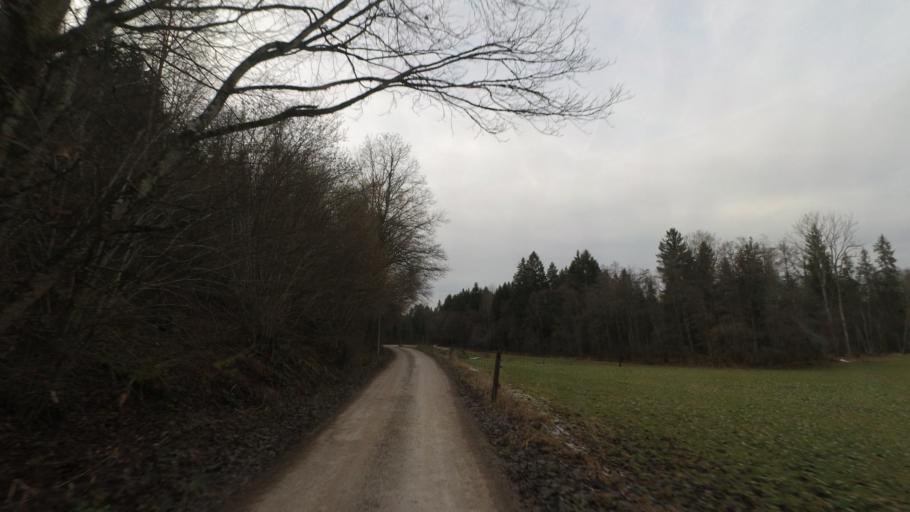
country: DE
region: Bavaria
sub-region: Upper Bavaria
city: Ubersee
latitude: 47.8094
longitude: 12.5172
